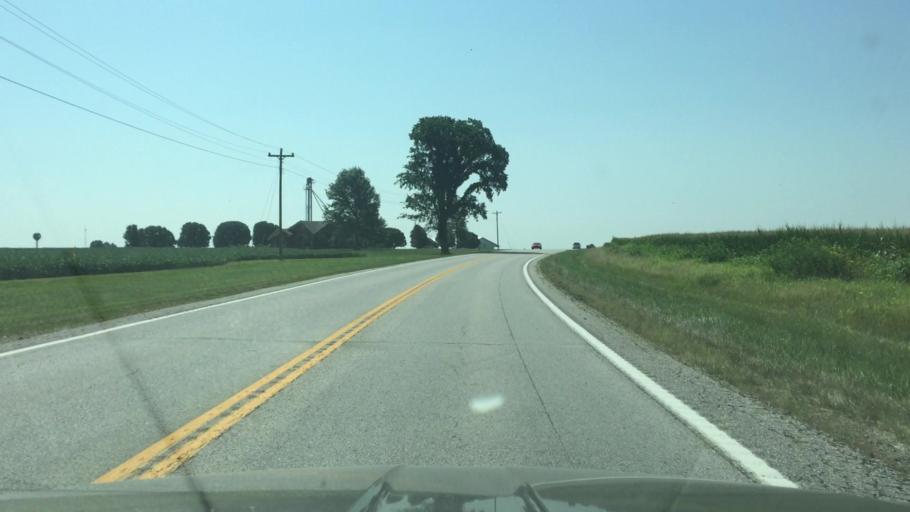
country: US
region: Missouri
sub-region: Moniteau County
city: Tipton
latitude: 38.6603
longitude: -92.8098
